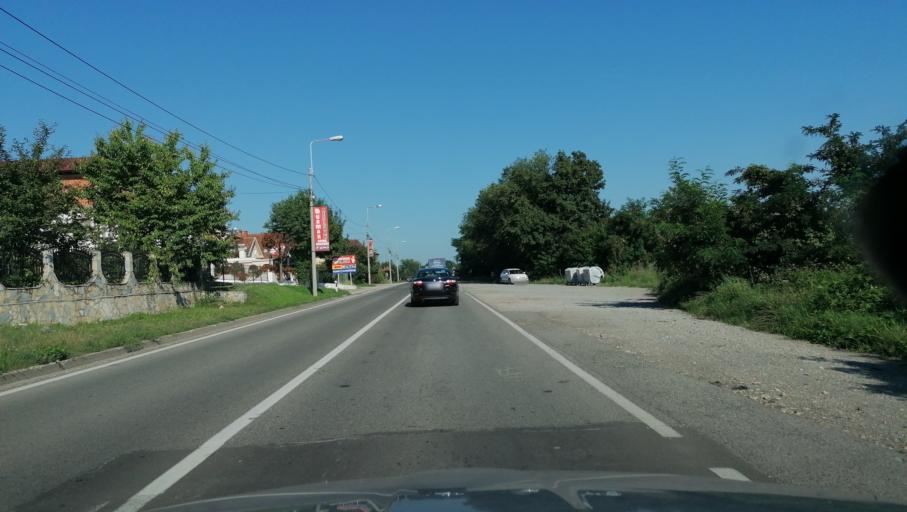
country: RS
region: Central Serbia
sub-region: Raski Okrug
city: Kraljevo
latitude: 43.7204
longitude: 20.6372
